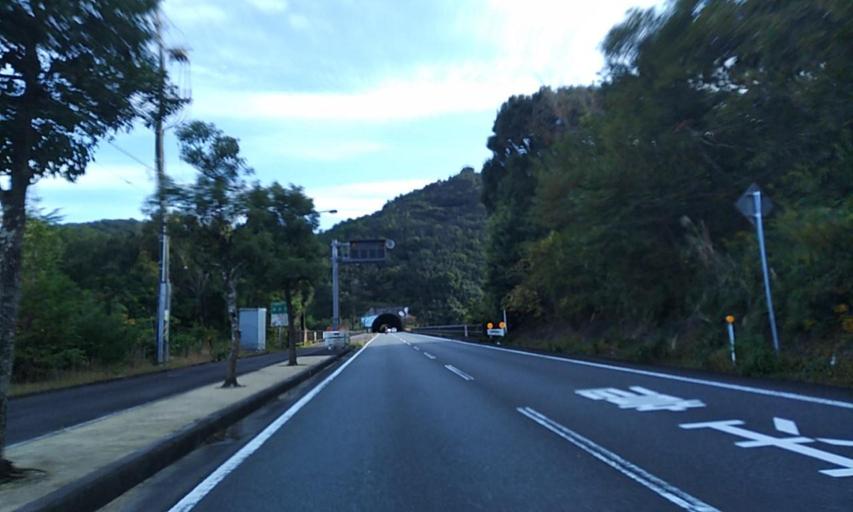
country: JP
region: Mie
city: Toba
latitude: 34.3672
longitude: 136.7939
